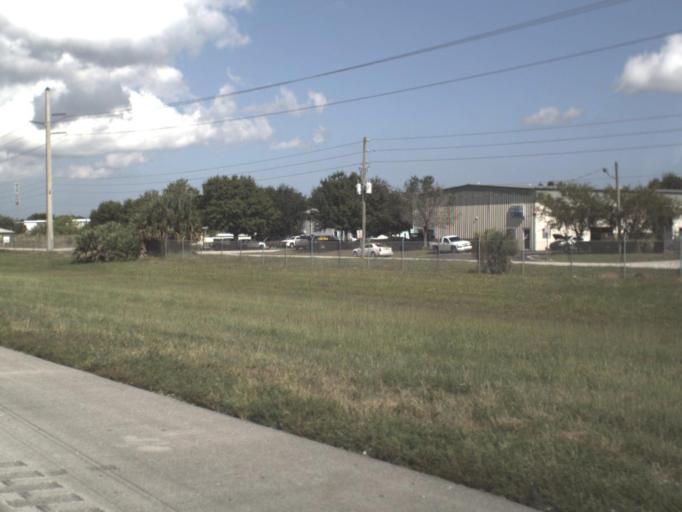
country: US
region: Florida
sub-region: Saint Lucie County
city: Port Saint Lucie
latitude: 27.3066
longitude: -80.3731
